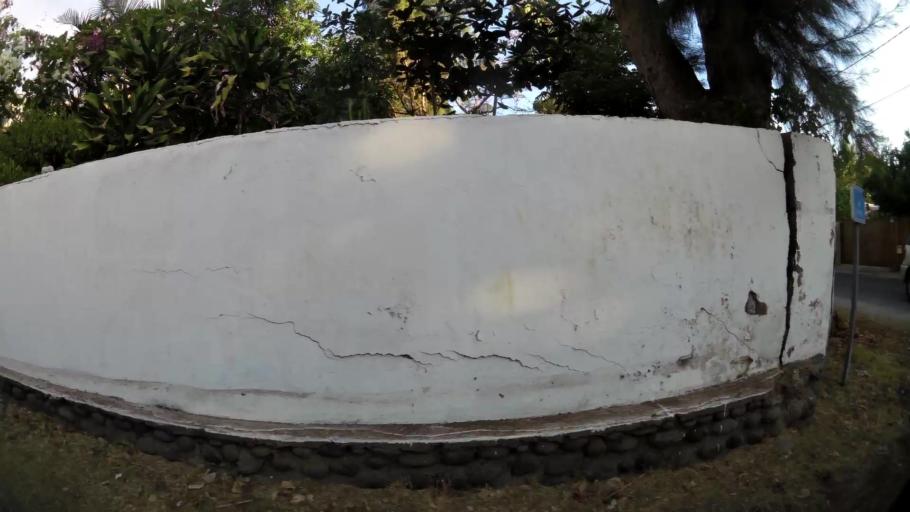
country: RE
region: Reunion
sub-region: Reunion
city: Saint-Paul
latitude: -21.0395
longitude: 55.2173
